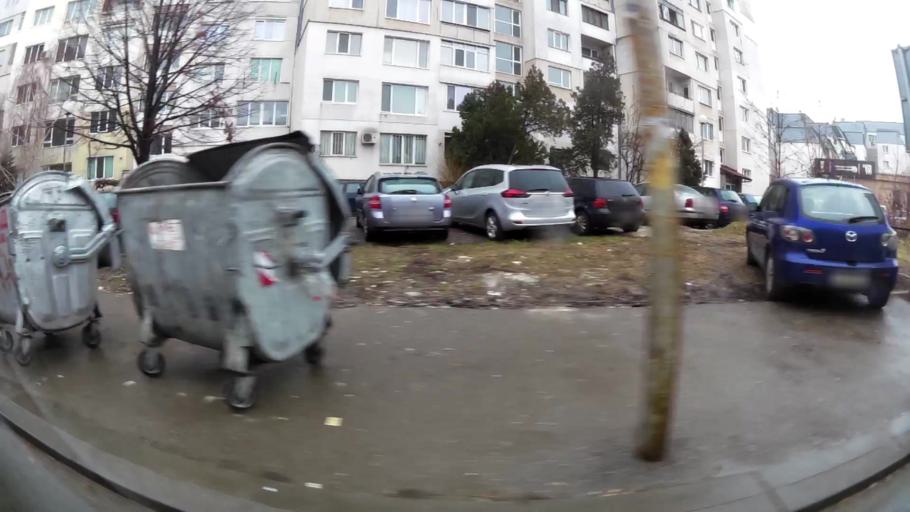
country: BG
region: Sofia-Capital
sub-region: Stolichna Obshtina
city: Sofia
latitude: 42.6264
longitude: 23.3784
